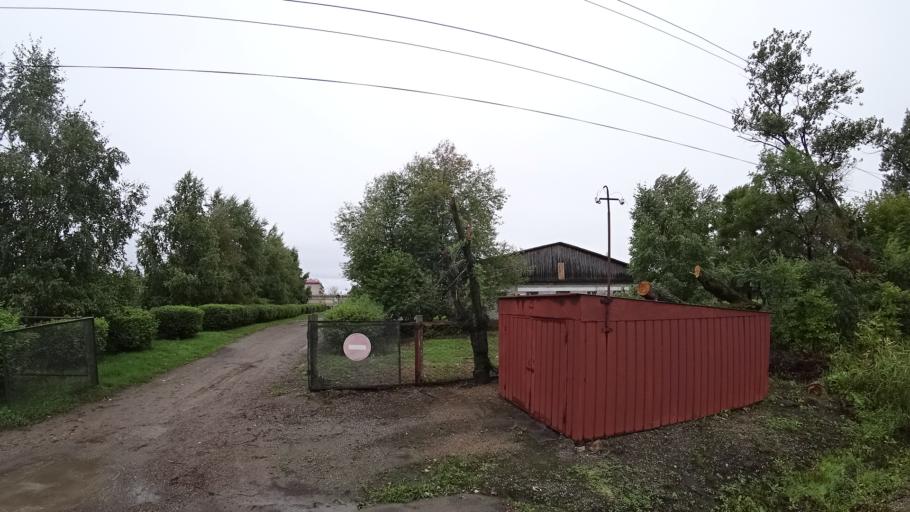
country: RU
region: Primorskiy
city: Monastyrishche
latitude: 44.2090
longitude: 132.4454
